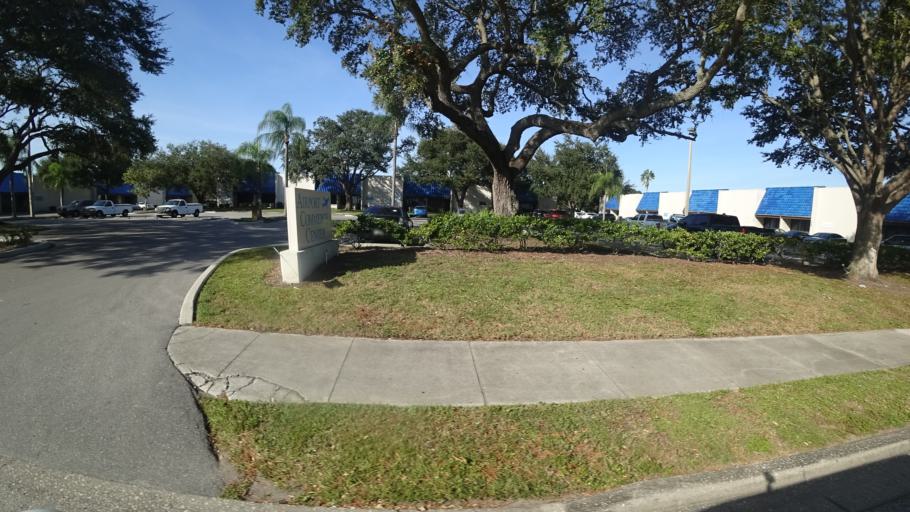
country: US
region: Florida
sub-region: Manatee County
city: Whitfield
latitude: 27.4038
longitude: -82.5486
